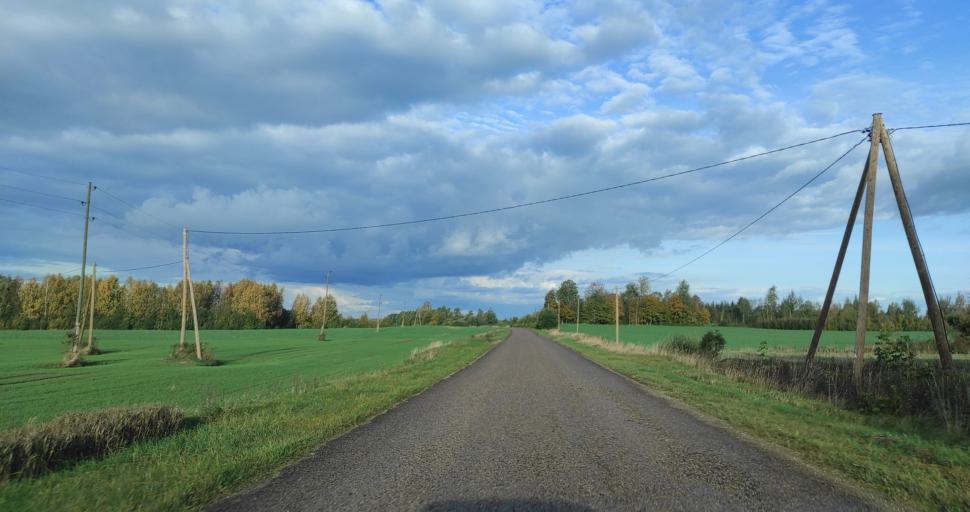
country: LV
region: Aizpute
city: Aizpute
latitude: 56.7782
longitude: 21.7775
